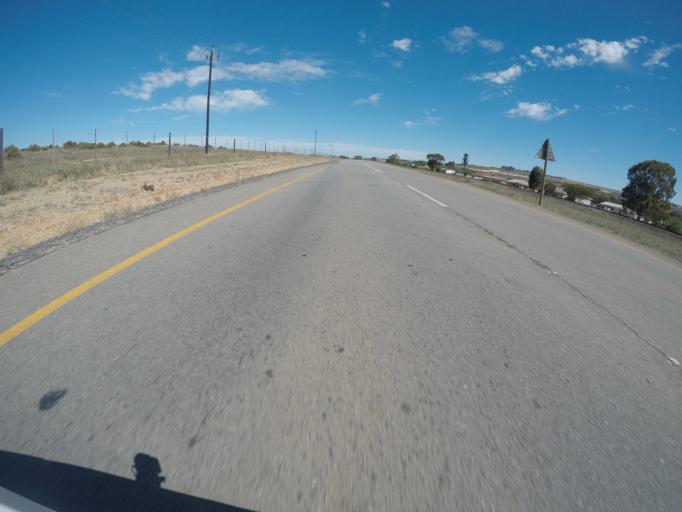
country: ZA
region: Western Cape
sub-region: West Coast District Municipality
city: Malmesbury
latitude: -33.4864
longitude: 18.6891
